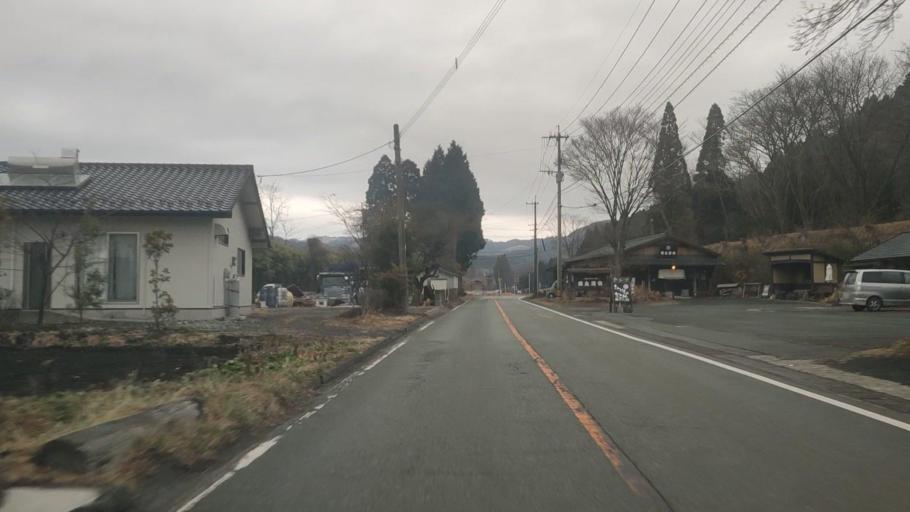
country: JP
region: Kumamoto
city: Aso
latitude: 32.8529
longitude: 131.1527
